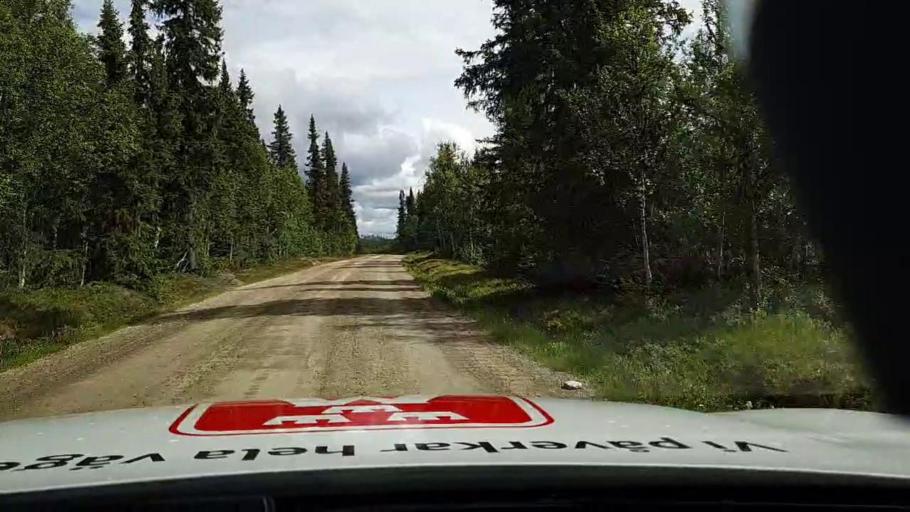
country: SE
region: Jaemtland
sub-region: Are Kommun
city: Jarpen
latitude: 62.5993
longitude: 13.3253
